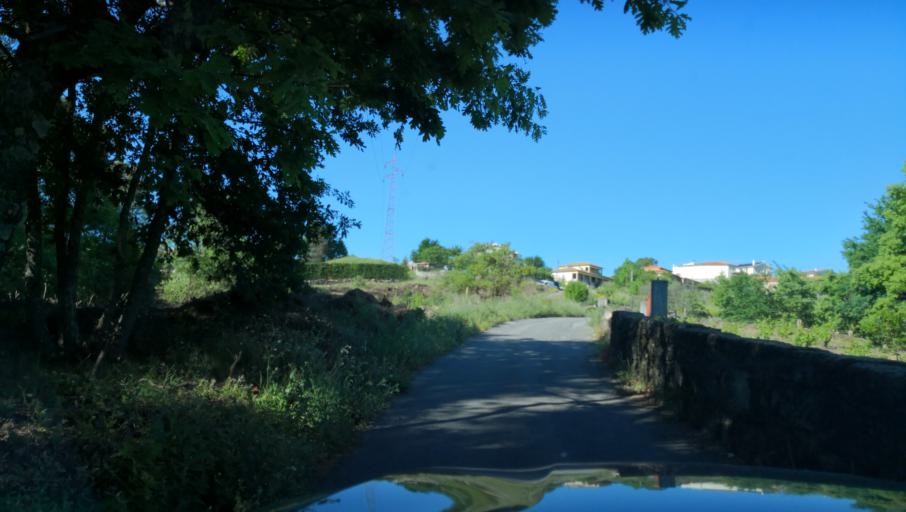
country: PT
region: Vila Real
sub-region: Vila Real
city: Vila Real
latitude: 41.3302
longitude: -7.7329
